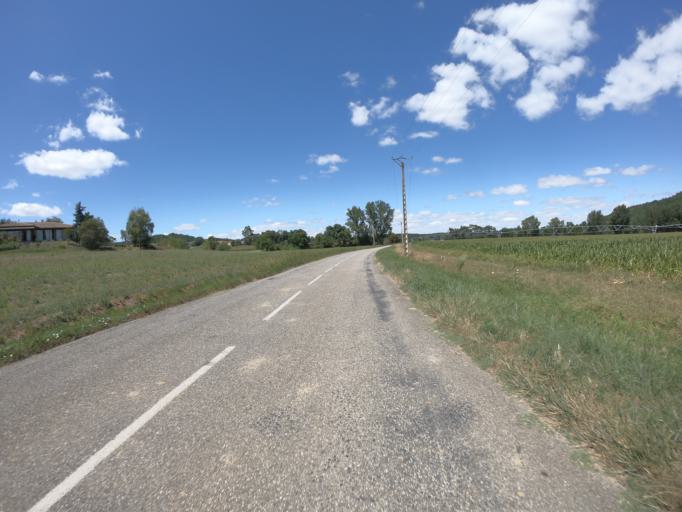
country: FR
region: Midi-Pyrenees
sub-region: Departement de l'Ariege
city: Verniolle
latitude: 43.0579
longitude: 1.7433
